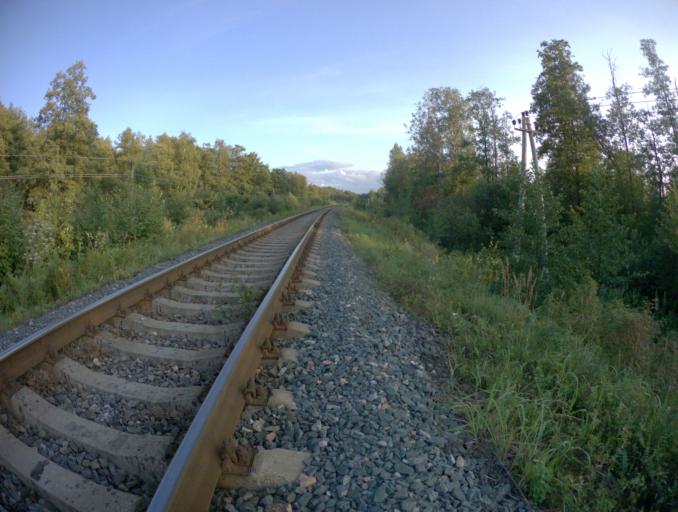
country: RU
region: Vladimir
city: Raduzhnyy
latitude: 56.0402
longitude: 40.3848
